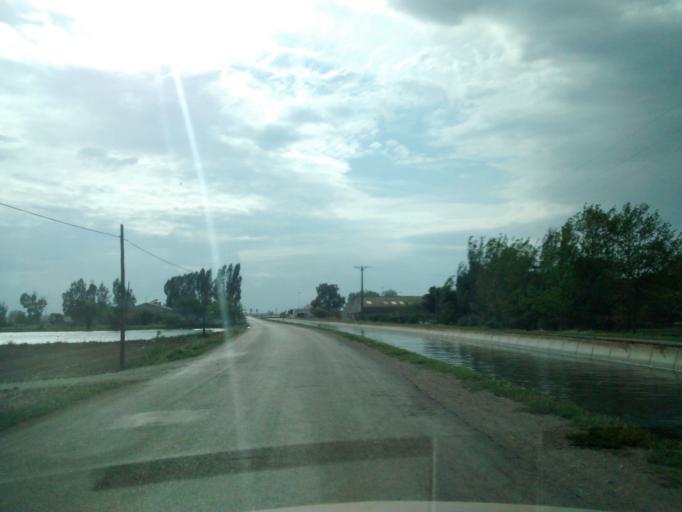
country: ES
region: Catalonia
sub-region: Provincia de Tarragona
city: Deltebre
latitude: 40.7025
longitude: 0.7378
